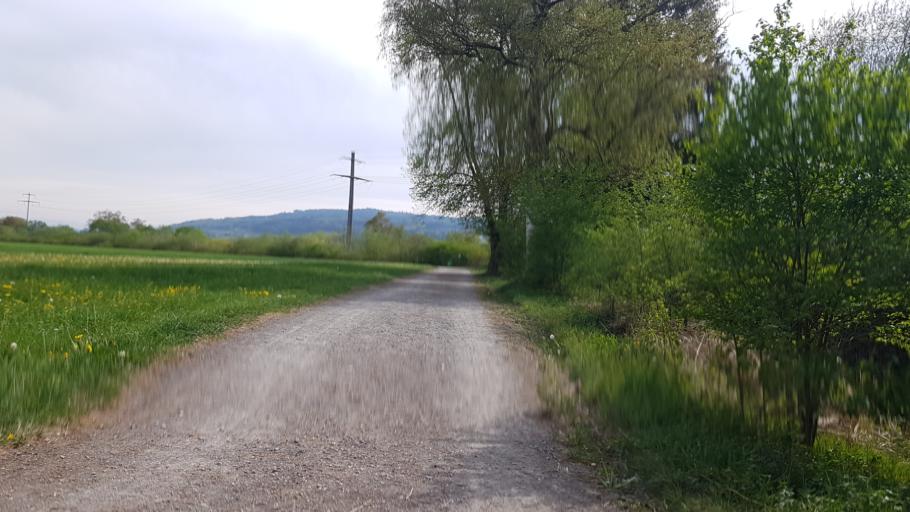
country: CH
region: Aargau
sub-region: Bezirk Kulm
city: Gontenschwil
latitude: 47.2799
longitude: 8.1509
